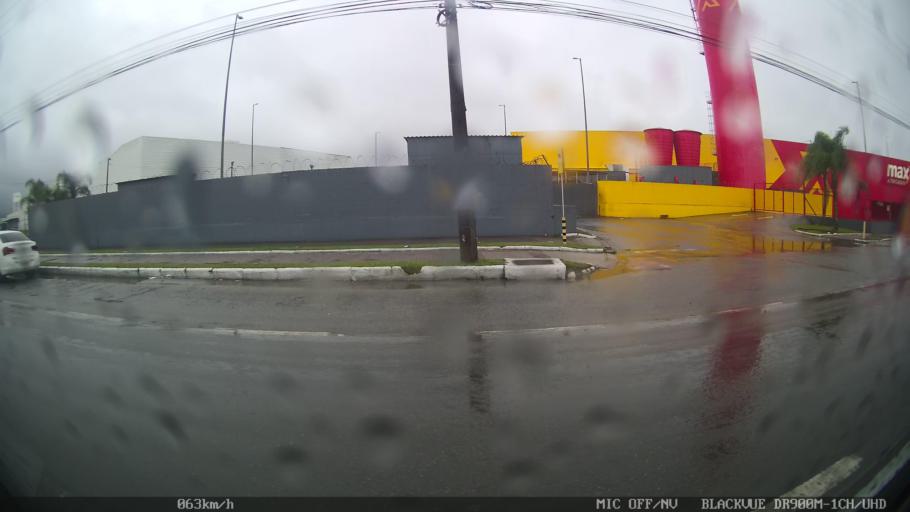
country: BR
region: Santa Catarina
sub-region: Itajai
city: Itajai
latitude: -26.9130
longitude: -48.6925
